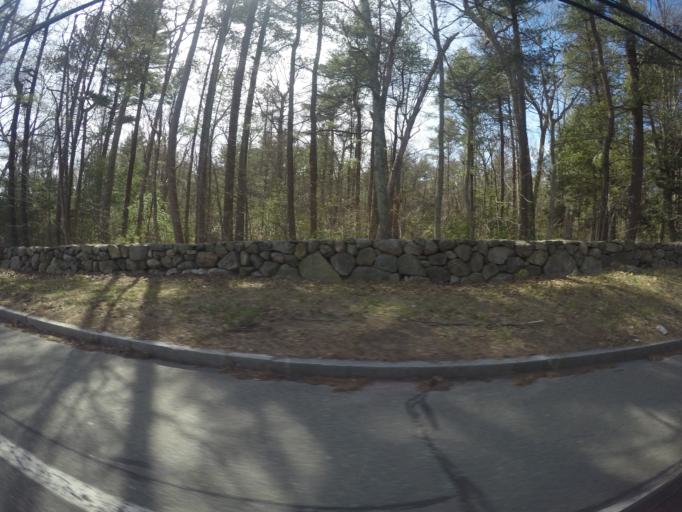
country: US
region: Massachusetts
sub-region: Bristol County
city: Easton
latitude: 42.0632
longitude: -71.0871
